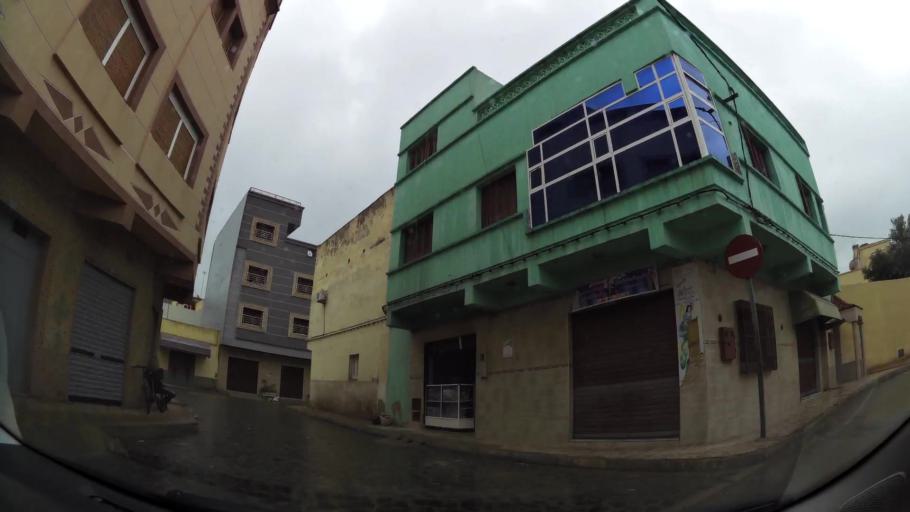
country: MA
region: Oriental
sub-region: Nador
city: Nador
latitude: 35.1737
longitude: -2.9397
